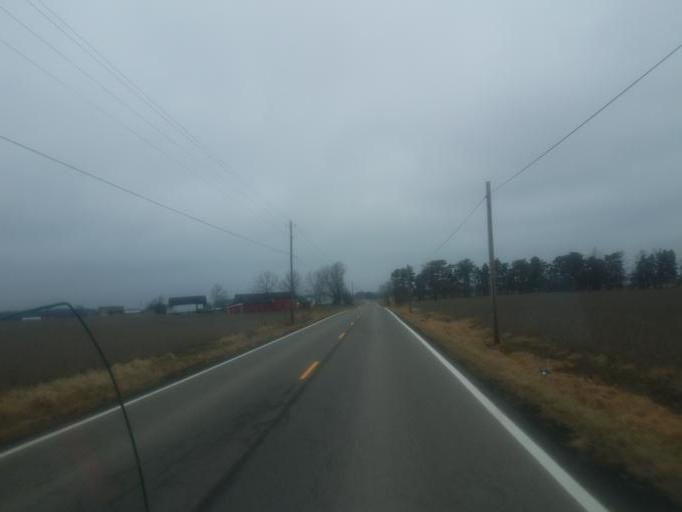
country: US
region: Ohio
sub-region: Richland County
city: Lincoln Heights
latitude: 40.9012
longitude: -82.4698
